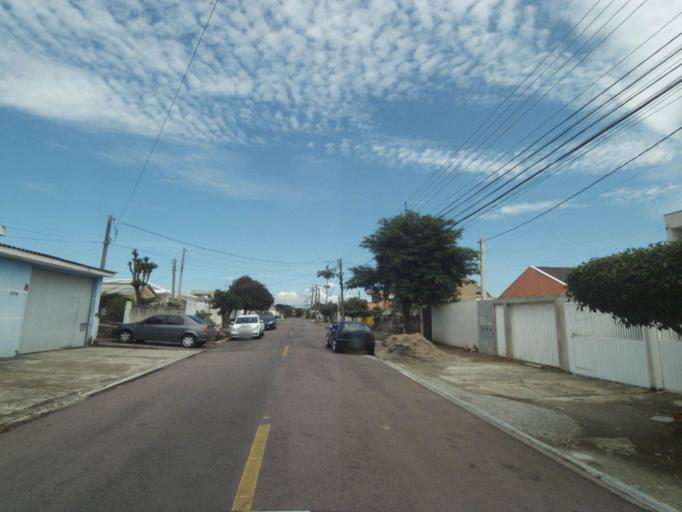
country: BR
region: Parana
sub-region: Pinhais
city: Pinhais
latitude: -25.4705
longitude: -49.1934
